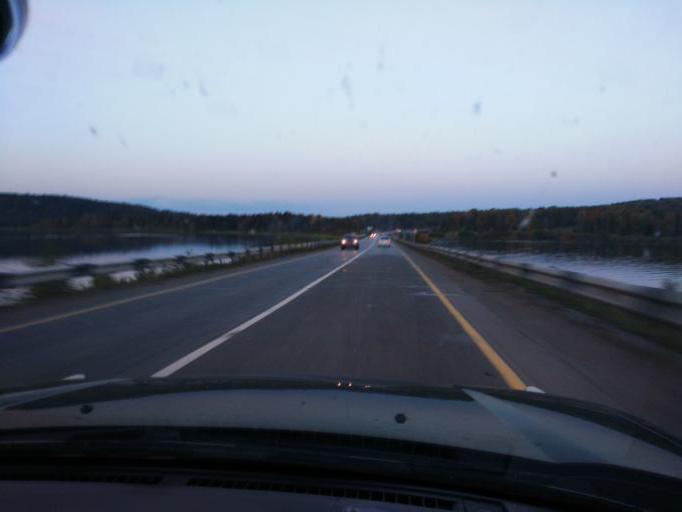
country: RU
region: Perm
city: Verkhnechusovskiye Gorodki
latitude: 58.2935
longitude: 56.8793
